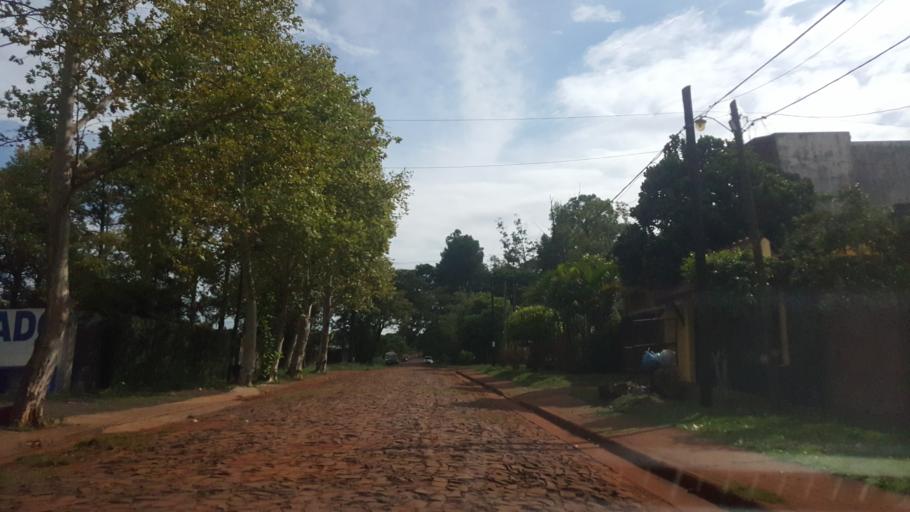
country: AR
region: Misiones
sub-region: Departamento de Capital
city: Posadas
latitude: -27.4021
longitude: -55.9189
